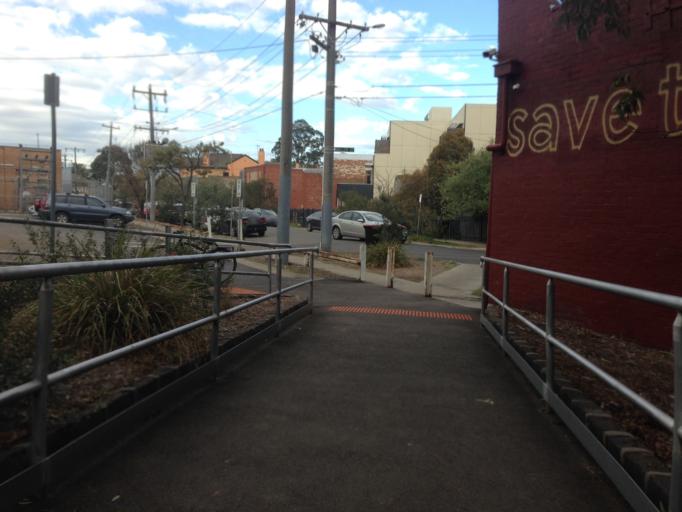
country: AU
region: Victoria
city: Alphington
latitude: -37.7787
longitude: 145.0312
